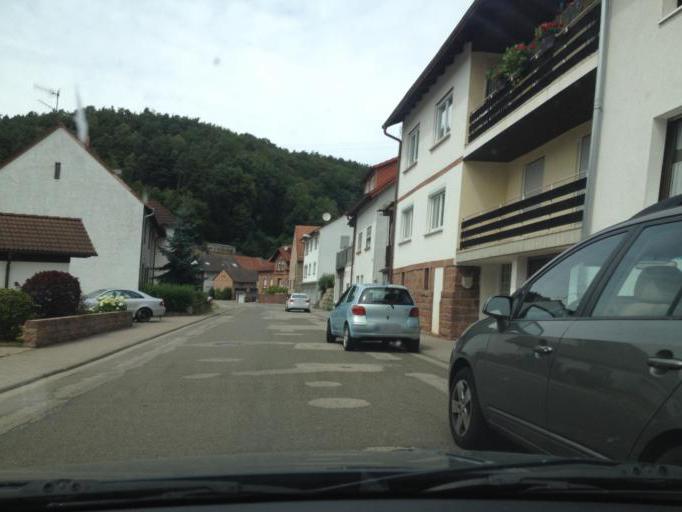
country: DE
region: Rheinland-Pfalz
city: Linden
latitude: 49.3504
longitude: 7.6473
